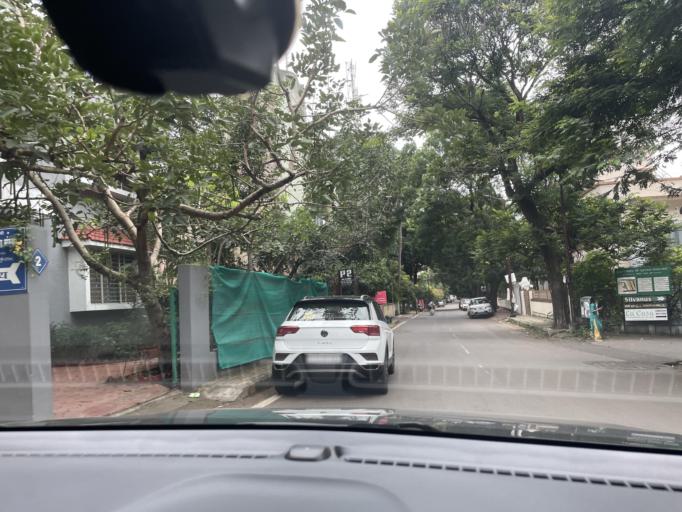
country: IN
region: Maharashtra
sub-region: Pune Division
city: Shivaji Nagar
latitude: 18.5334
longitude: 73.8113
